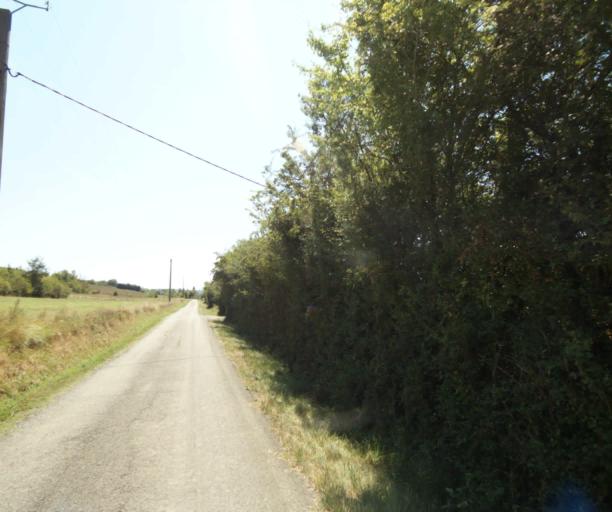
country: FR
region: Midi-Pyrenees
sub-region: Departement de la Haute-Garonne
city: Saint-Sulpice-sur-Leze
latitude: 43.3113
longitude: 1.3393
